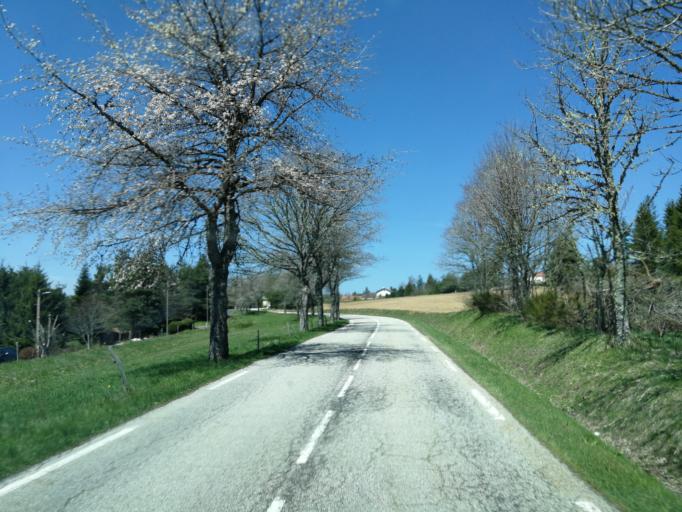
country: FR
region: Rhone-Alpes
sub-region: Departement de l'Ardeche
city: Saint-Agreve
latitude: 45.0641
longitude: 4.3918
